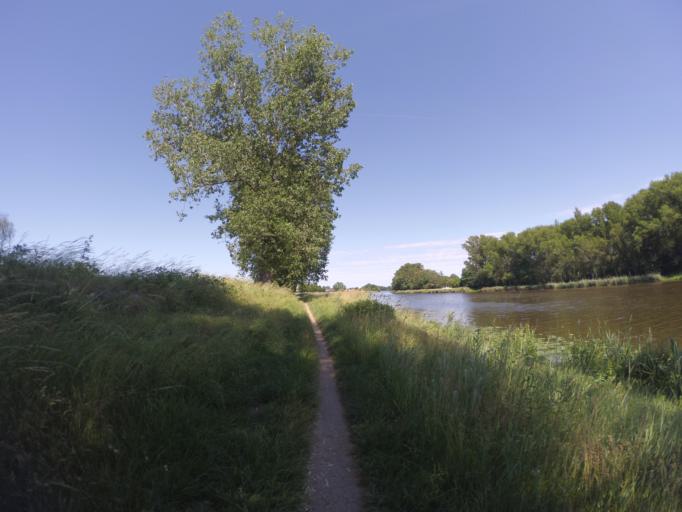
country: CZ
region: Central Bohemia
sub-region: Okres Nymburk
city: Sadska
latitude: 50.1705
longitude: 15.0011
